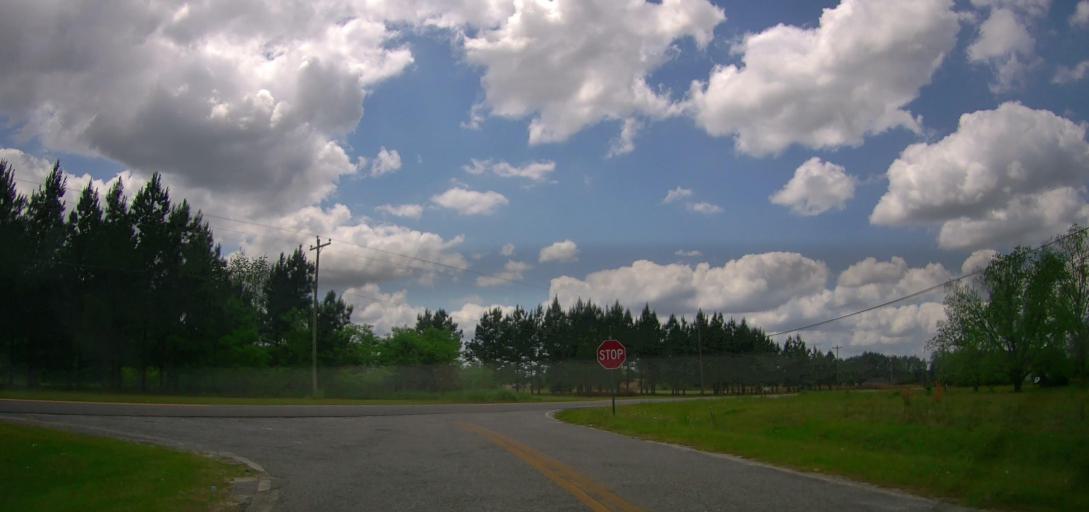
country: US
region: Georgia
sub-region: Laurens County
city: Dublin
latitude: 32.6011
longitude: -82.9520
